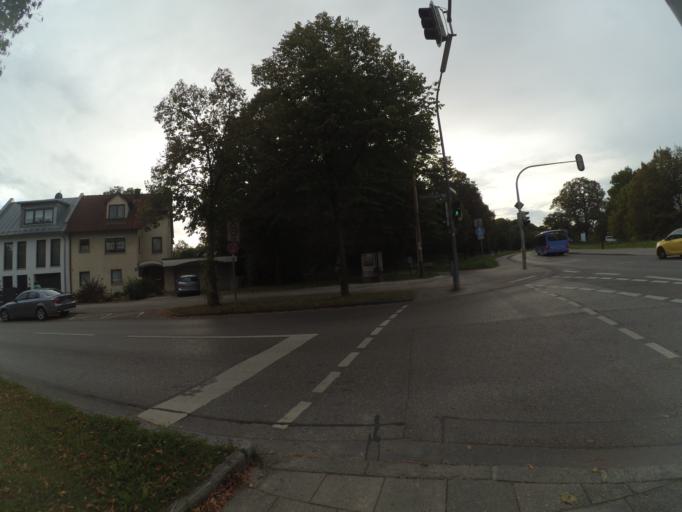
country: DE
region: Bavaria
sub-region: Upper Bavaria
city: Pasing
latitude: 48.1676
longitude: 11.5166
